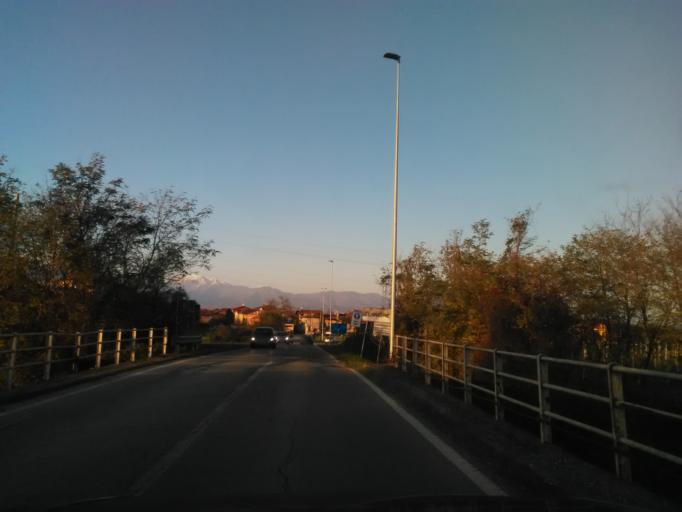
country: IT
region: Piedmont
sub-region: Provincia di Biella
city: Cerrione
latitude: 45.4654
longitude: 8.0696
